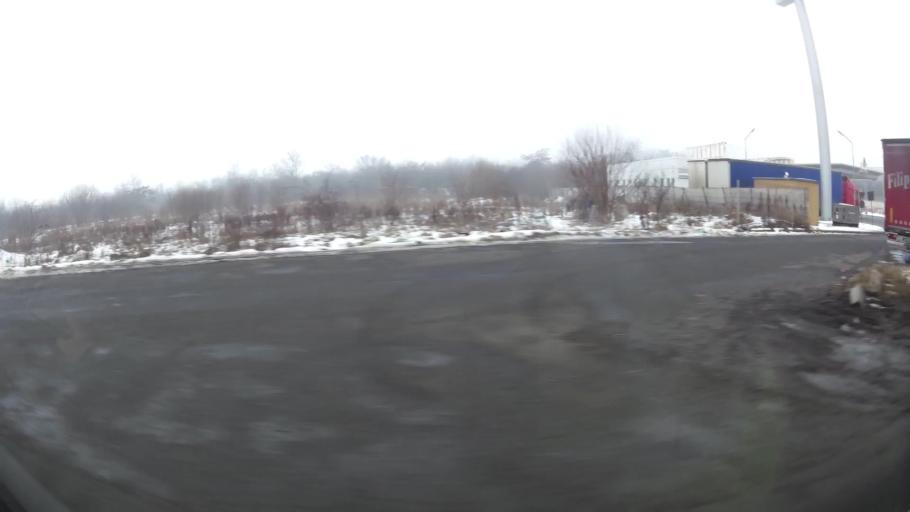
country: RO
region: Ilfov
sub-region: Comuna Chiajna
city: Chiajna
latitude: 44.4336
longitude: 25.9673
